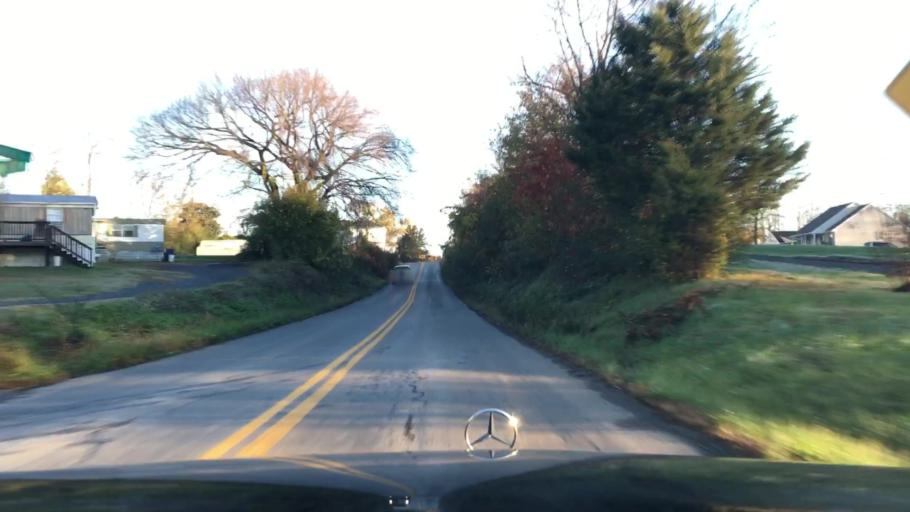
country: US
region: Virginia
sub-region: Campbell County
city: Timberlake
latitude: 37.3002
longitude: -79.2813
